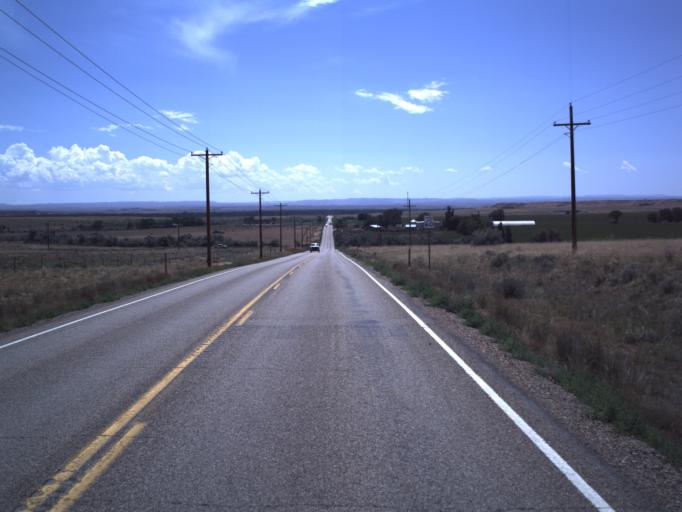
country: US
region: Utah
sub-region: Uintah County
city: Naples
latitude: 40.1550
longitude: -109.6642
